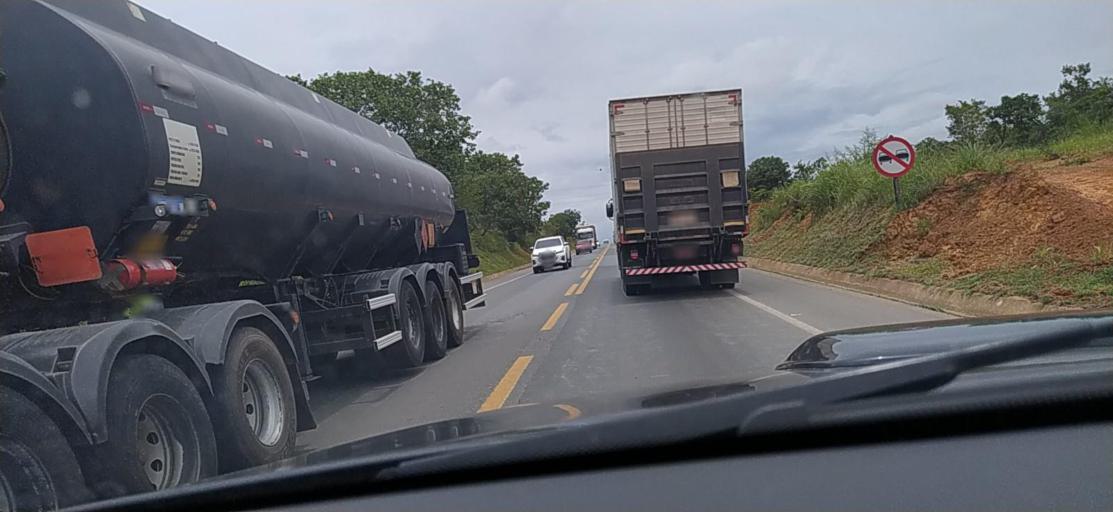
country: BR
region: Minas Gerais
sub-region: Curvelo
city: Curvelo
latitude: -18.7336
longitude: -44.4428
